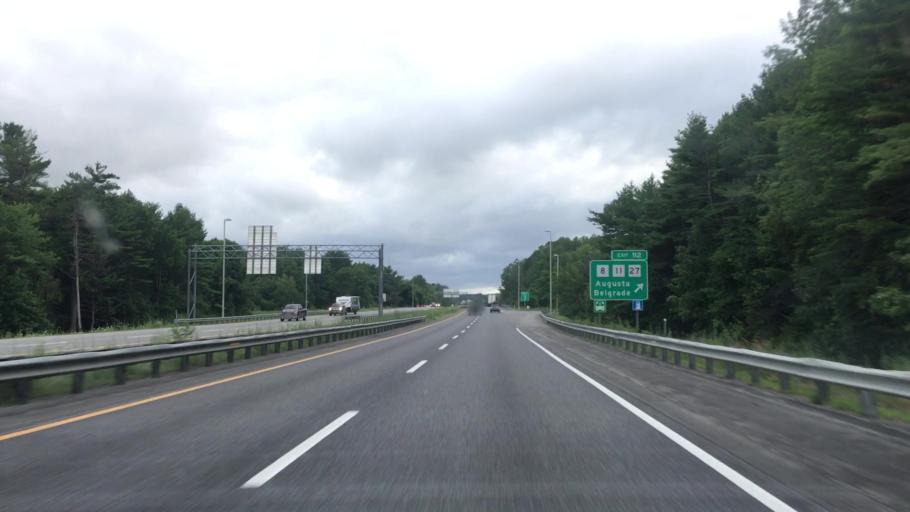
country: US
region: Maine
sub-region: Kennebec County
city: Augusta
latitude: 44.3483
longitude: -69.7908
